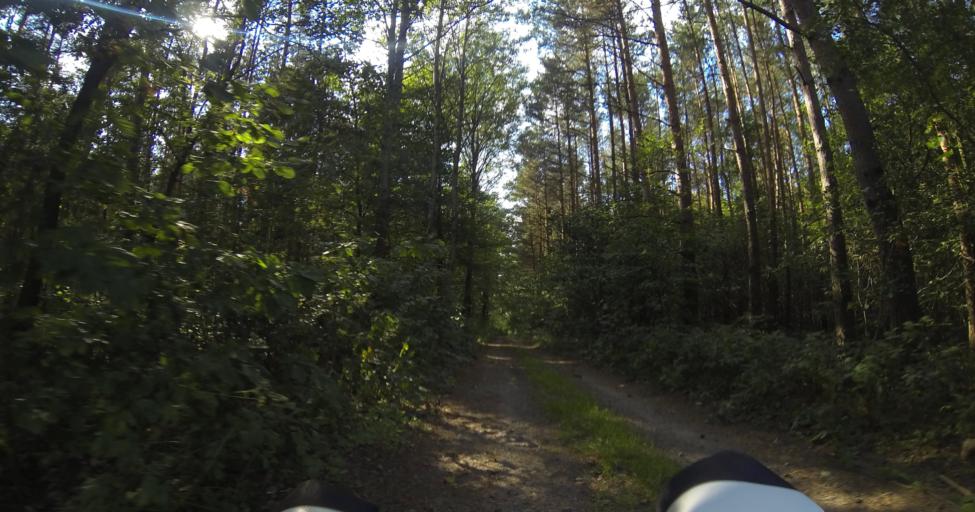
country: DE
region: Saxony
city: Ebersbach
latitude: 51.1978
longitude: 13.6612
